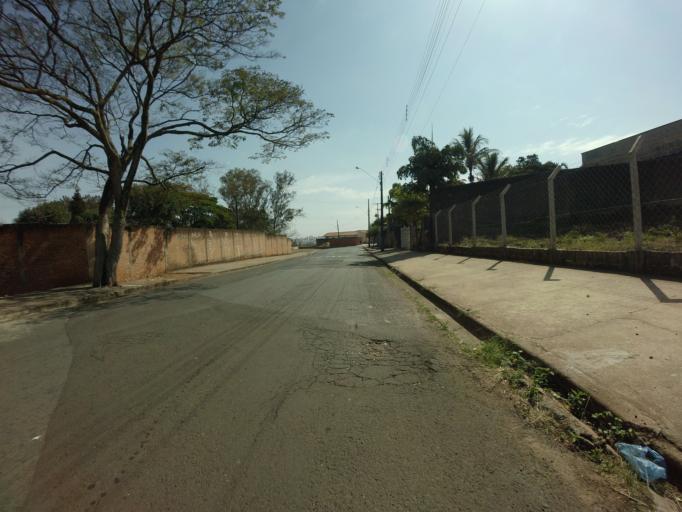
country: BR
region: Sao Paulo
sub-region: Piracicaba
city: Piracicaba
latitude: -22.7601
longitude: -47.5991
